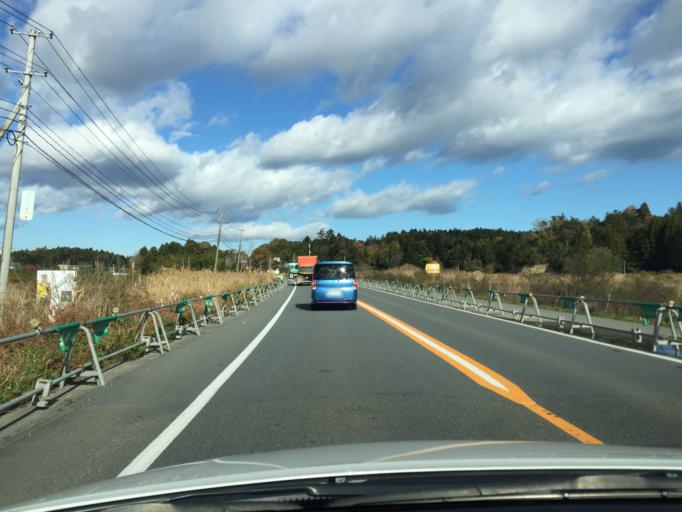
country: JP
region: Fukushima
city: Namie
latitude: 37.4679
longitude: 141.0093
